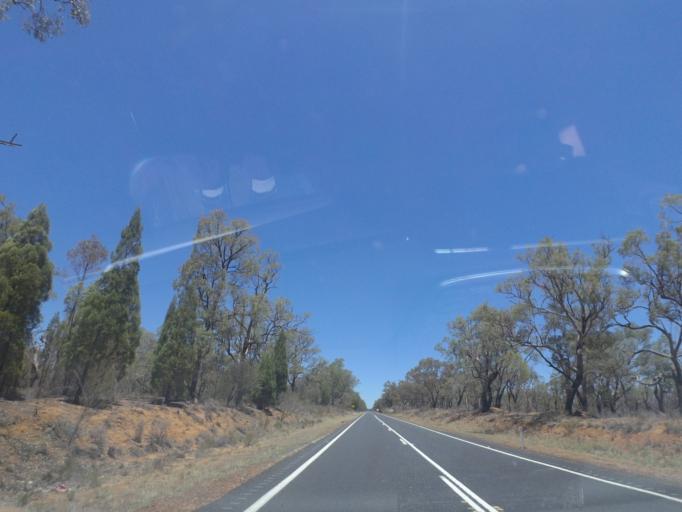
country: AU
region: New South Wales
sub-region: Warrumbungle Shire
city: Coonabarabran
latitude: -30.8553
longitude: 149.4563
